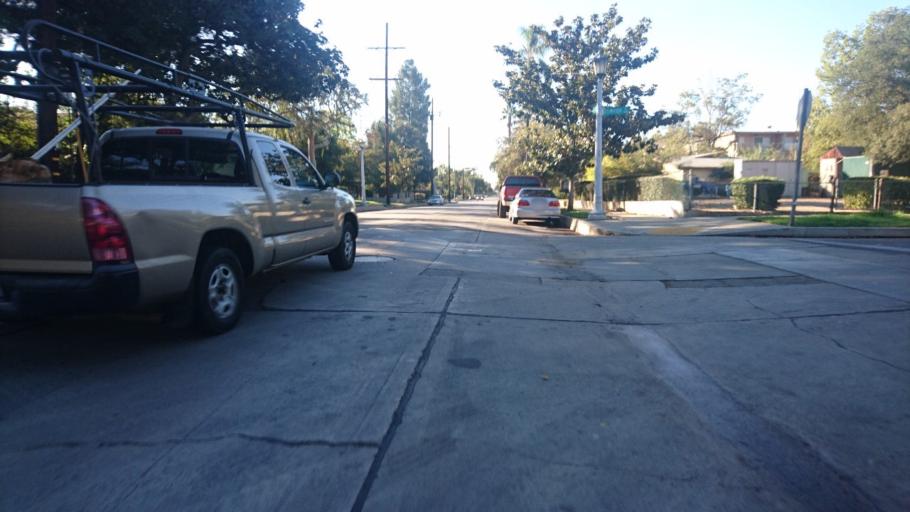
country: US
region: California
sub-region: Los Angeles County
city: East Pasadena
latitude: 34.1435
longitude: -118.0988
